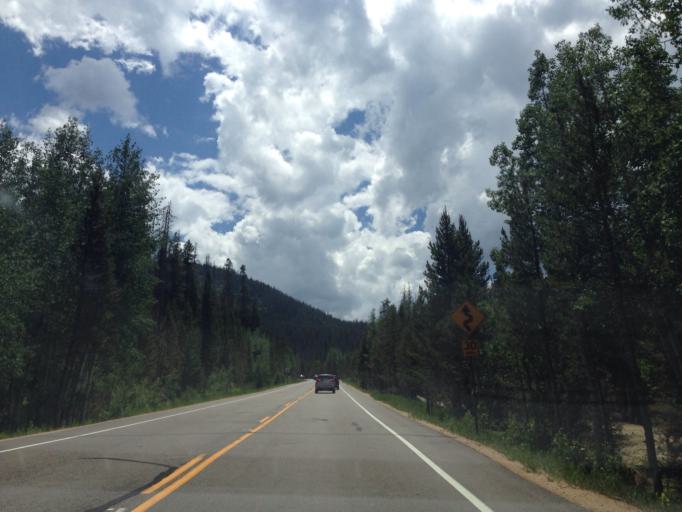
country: US
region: Colorado
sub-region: Larimer County
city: Estes Park
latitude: 40.6189
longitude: -105.8186
